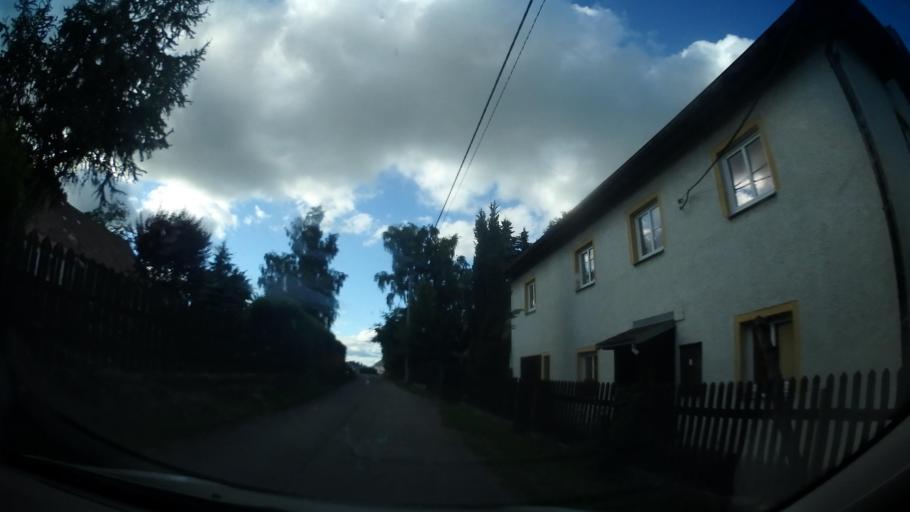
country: CZ
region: Vysocina
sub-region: Okres Zd'ar nad Sazavou
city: Jimramov
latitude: 49.6060
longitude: 16.1874
